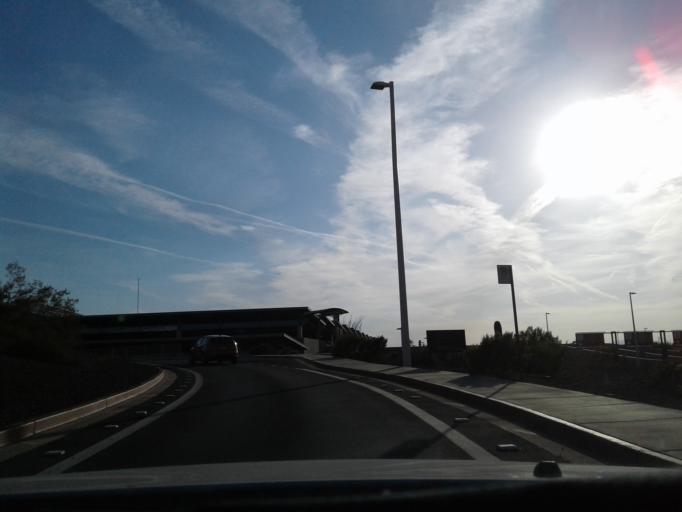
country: US
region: Arizona
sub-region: Maricopa County
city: Phoenix
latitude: 33.4319
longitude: -112.0438
